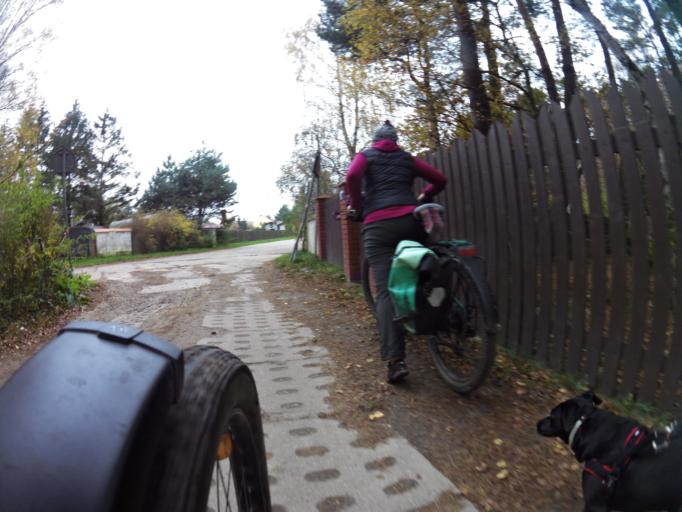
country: PL
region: Pomeranian Voivodeship
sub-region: Powiat pucki
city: Krokowa
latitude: 54.8289
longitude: 18.0957
